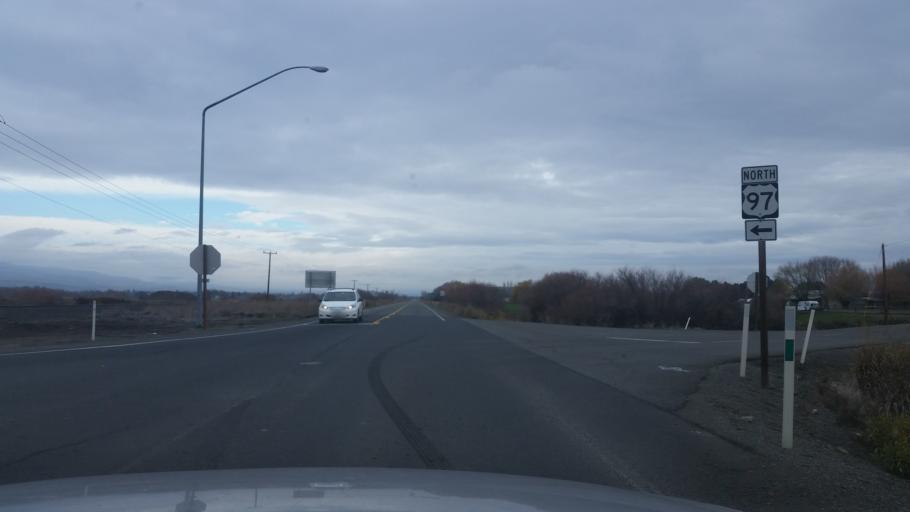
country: US
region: Washington
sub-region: Kittitas County
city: Ellensburg
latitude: 47.0219
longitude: -120.5924
